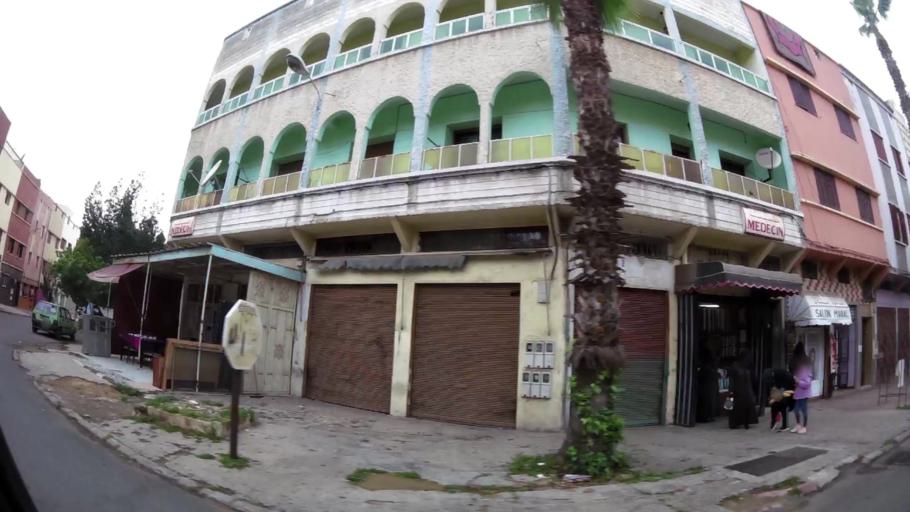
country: MA
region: Grand Casablanca
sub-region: Mohammedia
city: Mohammedia
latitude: 33.6818
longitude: -7.3953
